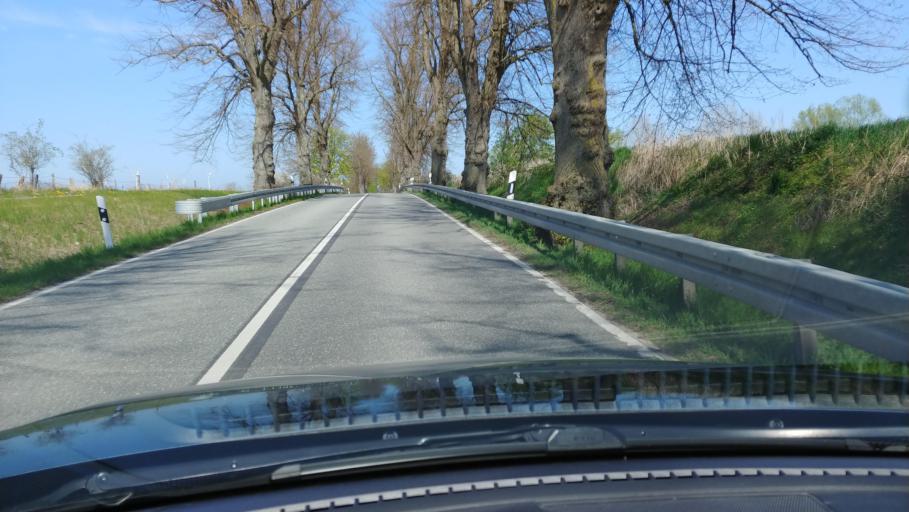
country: DE
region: Mecklenburg-Vorpommern
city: Muhlen Eichsen
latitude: 53.7645
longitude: 11.2608
